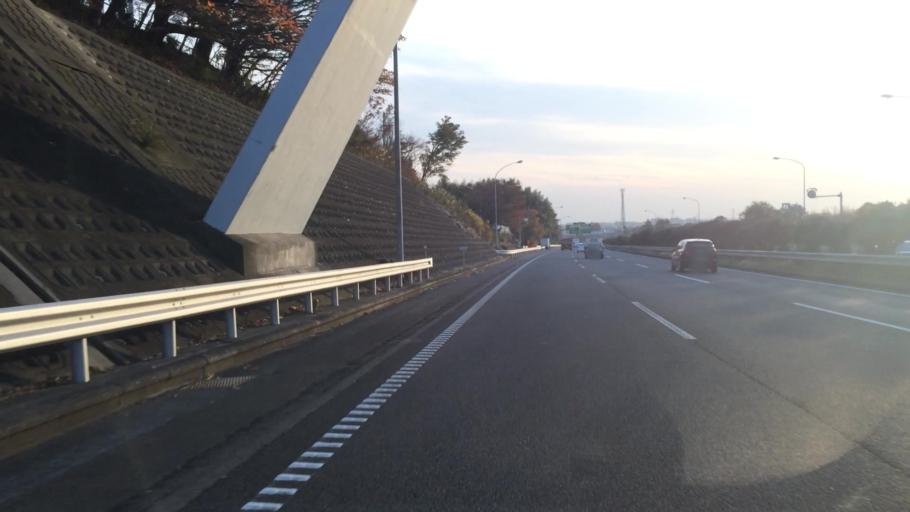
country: JP
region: Kanagawa
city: Yokohama
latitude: 35.5325
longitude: 139.5997
